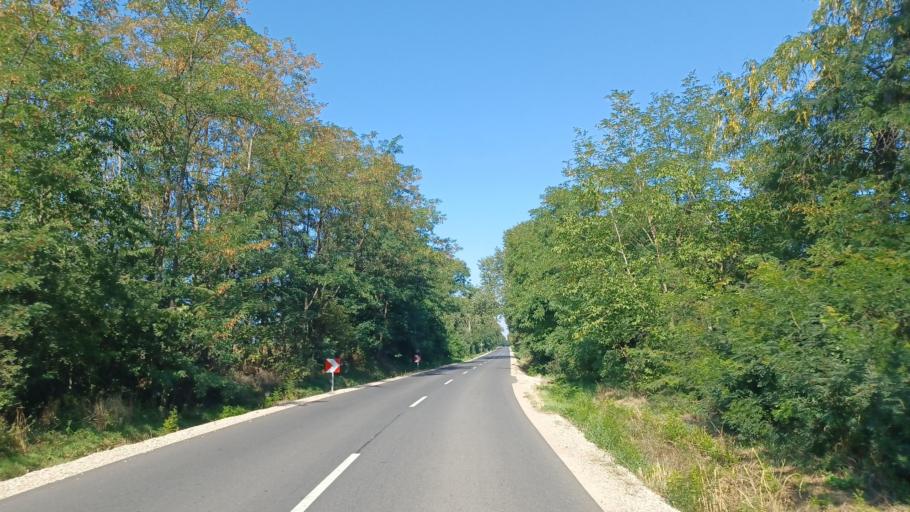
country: HU
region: Fejer
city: Cece
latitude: 46.7527
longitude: 18.6692
